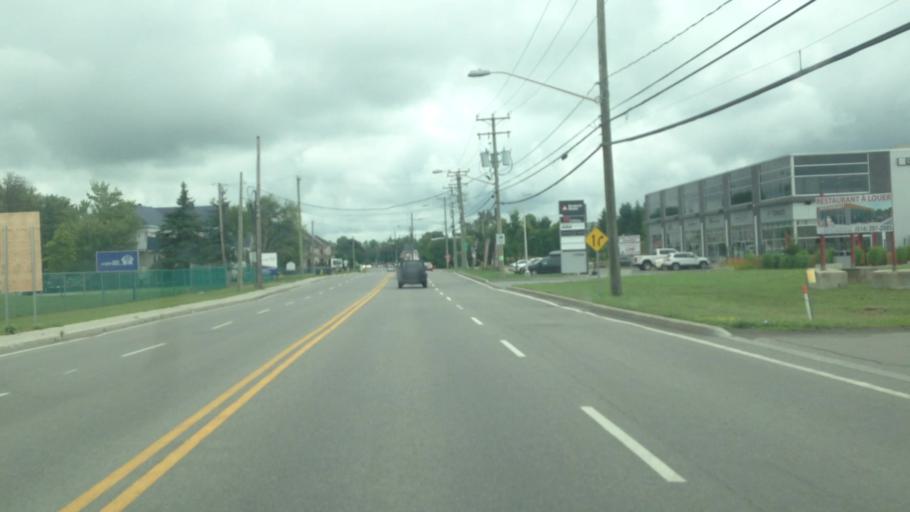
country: CA
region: Quebec
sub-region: Laurentides
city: Blainville
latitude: 45.6962
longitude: -73.9326
